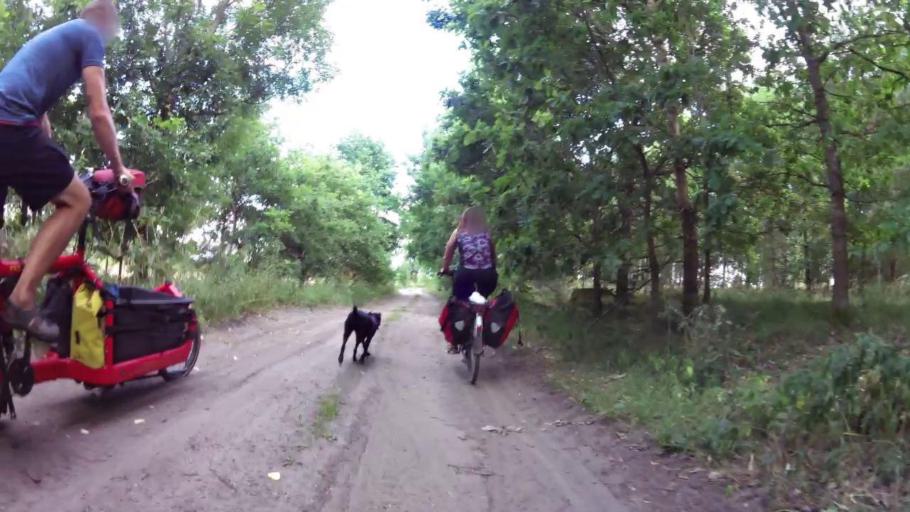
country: PL
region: West Pomeranian Voivodeship
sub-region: Powiat swidwinski
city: Swidwin
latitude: 53.6751
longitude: 15.7343
